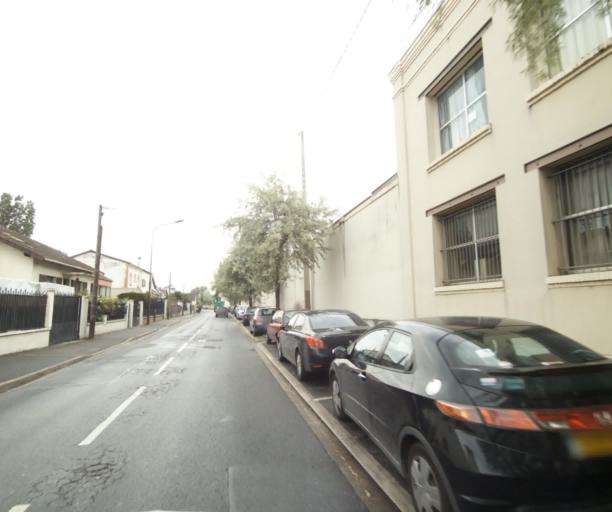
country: FR
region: Ile-de-France
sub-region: Departement du Val-d'Oise
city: Bezons
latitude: 48.9317
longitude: 2.2271
